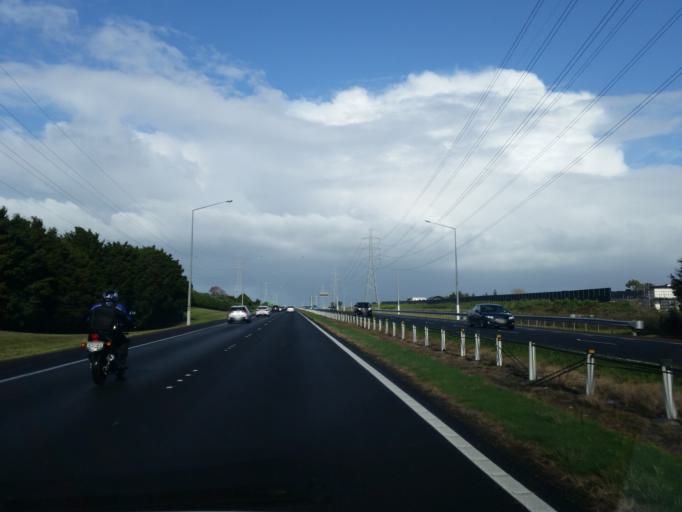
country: NZ
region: Auckland
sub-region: Auckland
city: Papakura
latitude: -37.0633
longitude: 174.9250
